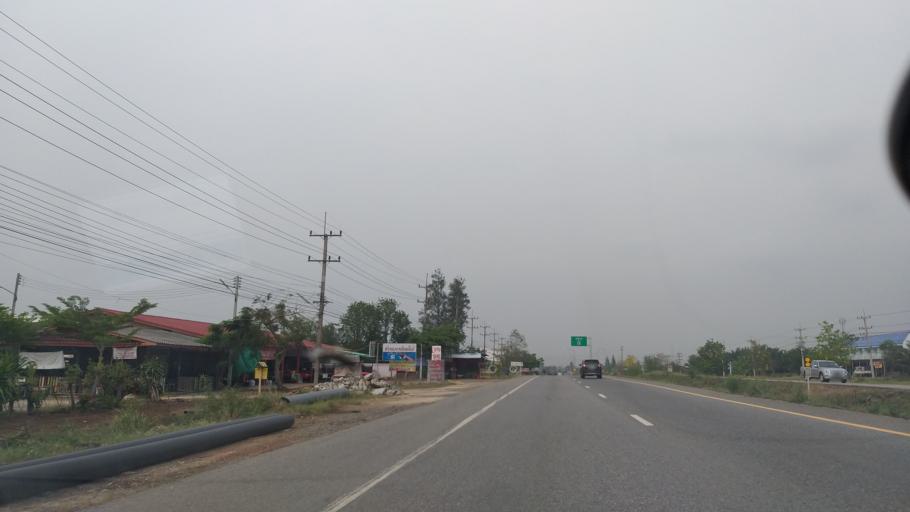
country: TH
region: Chon Buri
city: Ban Bueng
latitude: 13.2662
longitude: 101.2497
